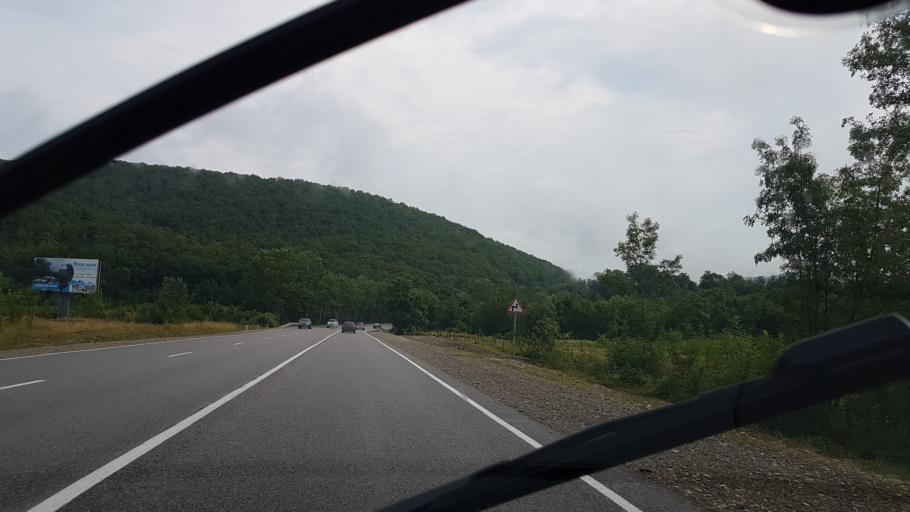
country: RU
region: Krasnodarskiy
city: Lermontovo
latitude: 44.4618
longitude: 38.8097
